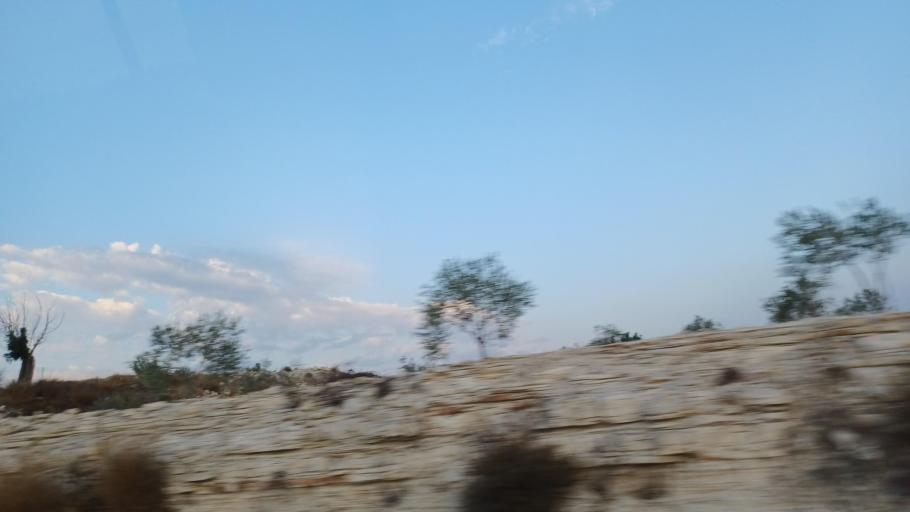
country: CY
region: Limassol
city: Pano Polemidia
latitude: 34.7588
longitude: 32.9697
